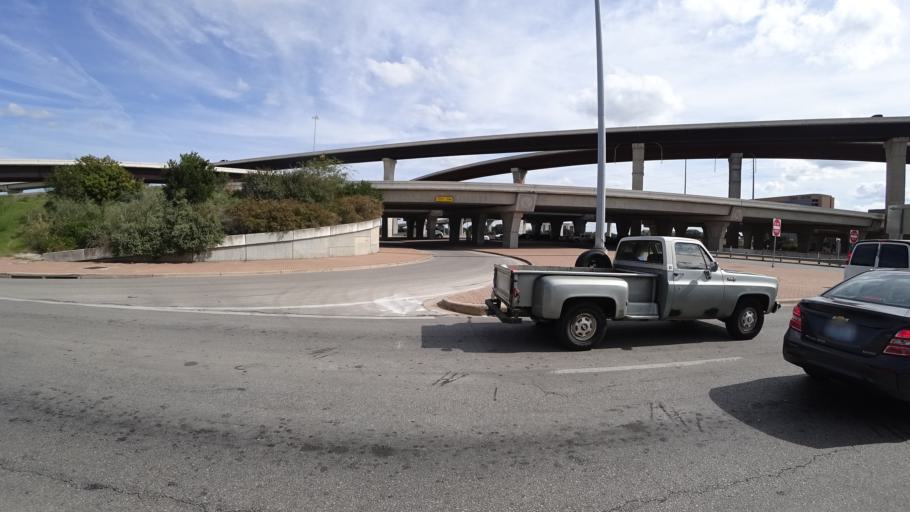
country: US
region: Texas
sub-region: Travis County
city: Austin
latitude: 30.2174
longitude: -97.7516
